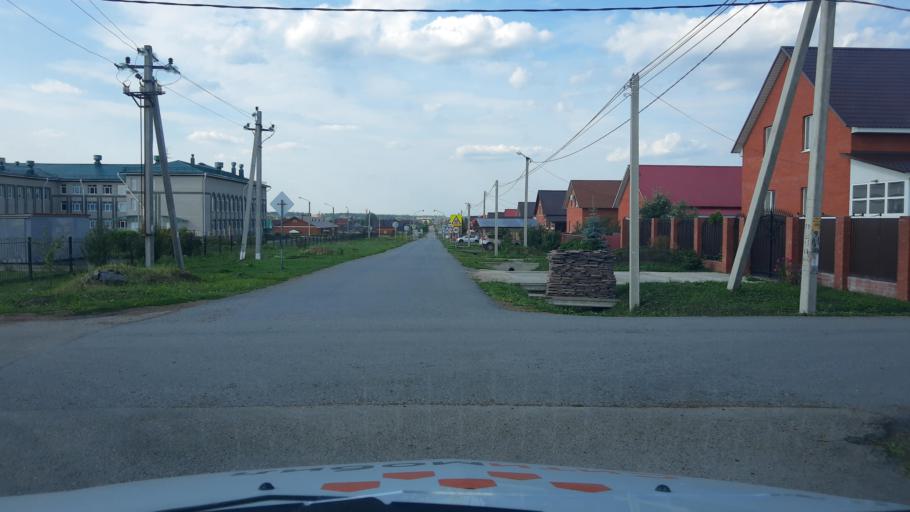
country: RU
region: Bashkortostan
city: Kabakovo
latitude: 54.6551
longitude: 56.2125
